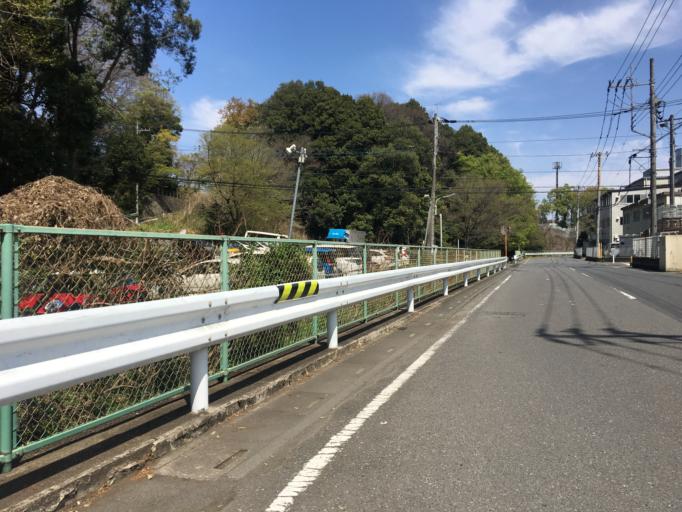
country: JP
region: Saitama
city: Shiki
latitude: 35.8217
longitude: 139.5489
